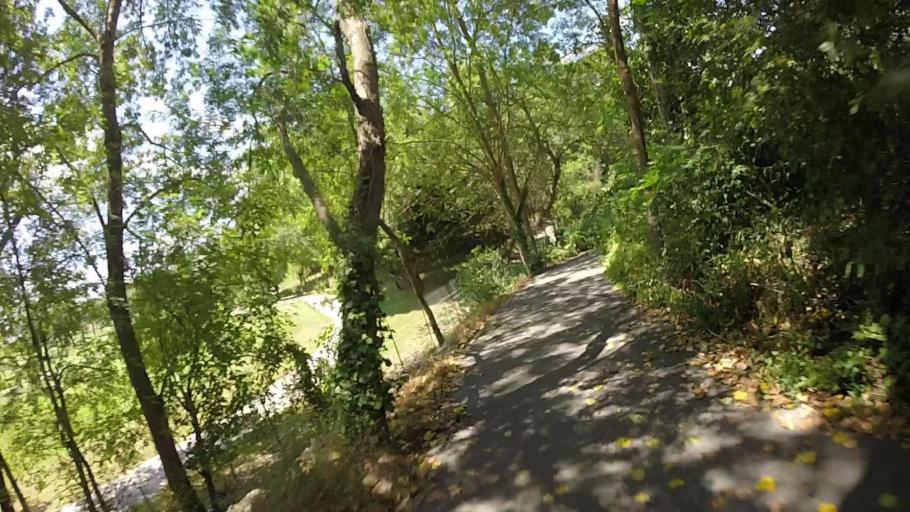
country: FR
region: Provence-Alpes-Cote d'Azur
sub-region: Departement des Alpes-Maritimes
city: Vallauris
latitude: 43.6151
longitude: 7.0419
